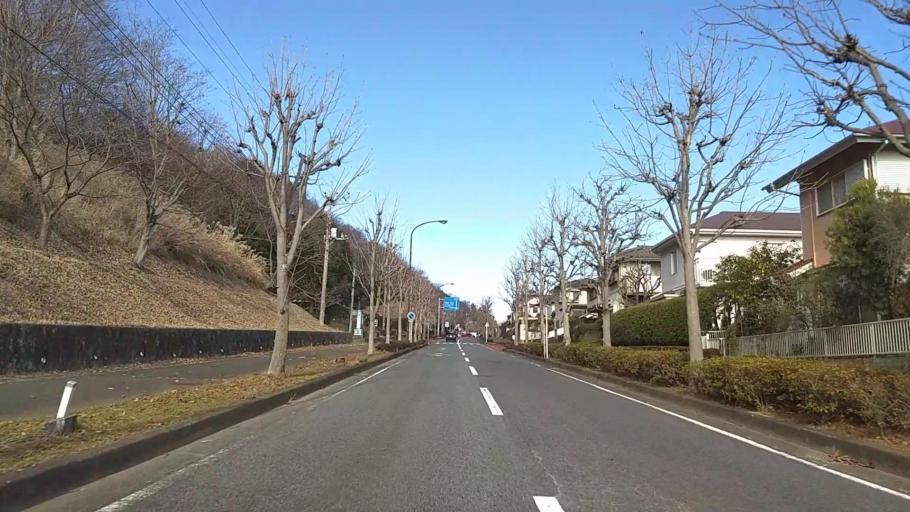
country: JP
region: Kanagawa
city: Atsugi
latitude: 35.4458
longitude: 139.3051
